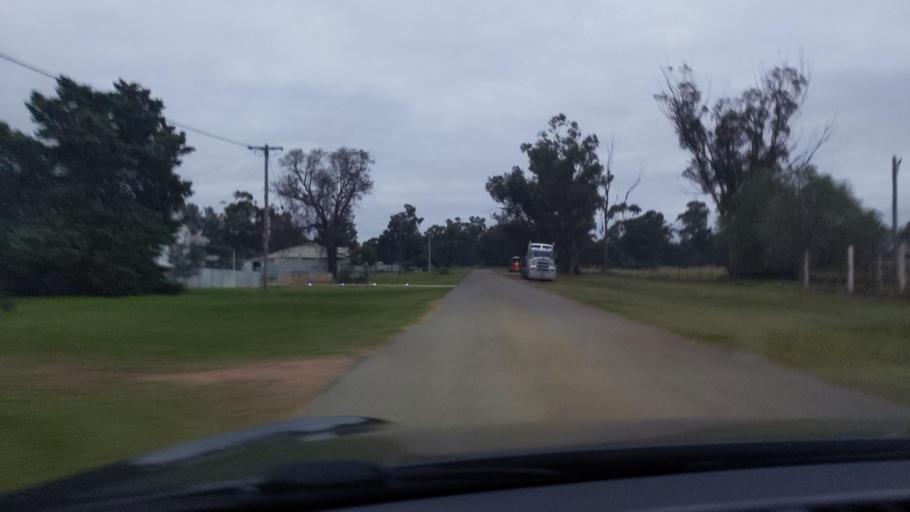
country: AU
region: New South Wales
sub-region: Narrandera
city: Narrandera
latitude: -34.7358
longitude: 146.7833
